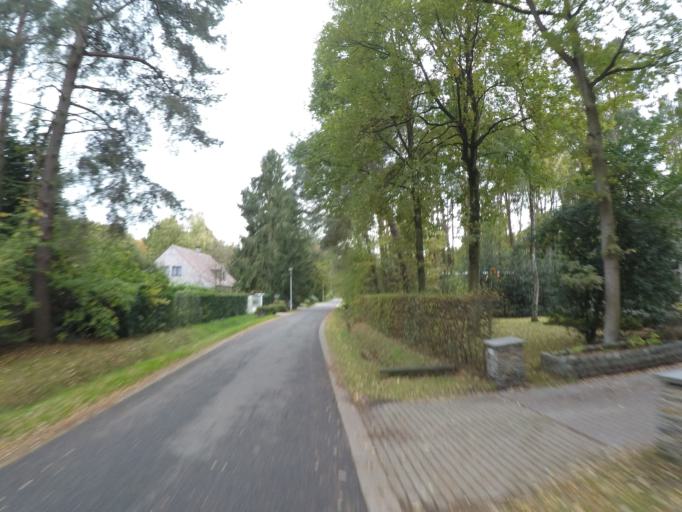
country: BE
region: Flanders
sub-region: Provincie Antwerpen
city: Zoersel
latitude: 51.2629
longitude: 4.6840
